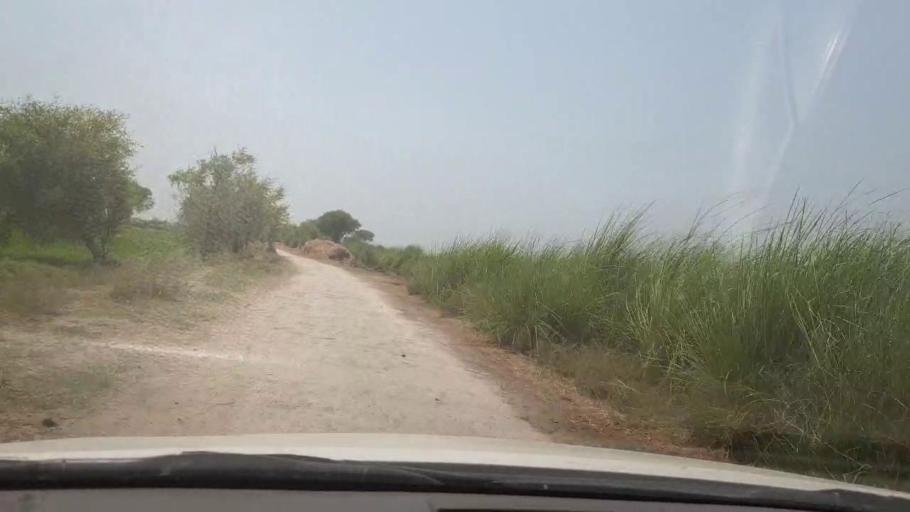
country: PK
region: Sindh
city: Shikarpur
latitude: 28.0813
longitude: 68.5526
